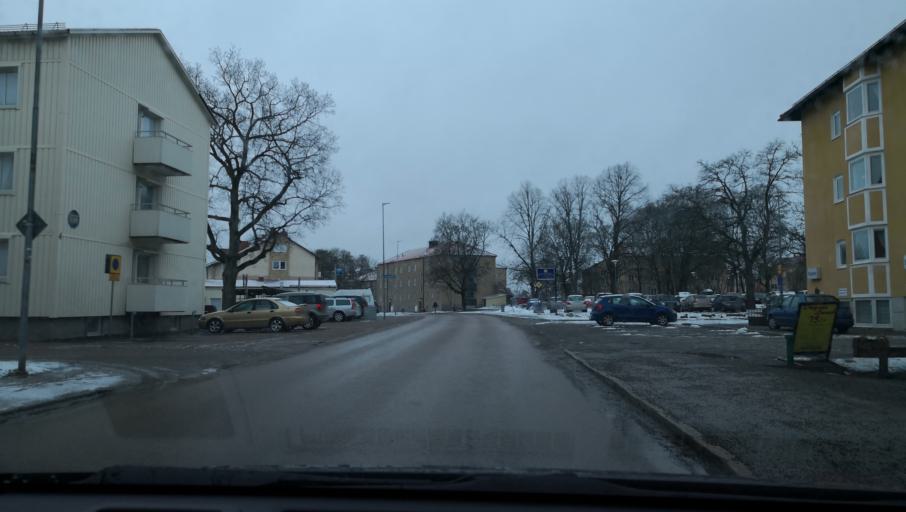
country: SE
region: Vaestmanland
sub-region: Kopings Kommun
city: Koping
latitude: 59.5221
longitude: 15.9897
